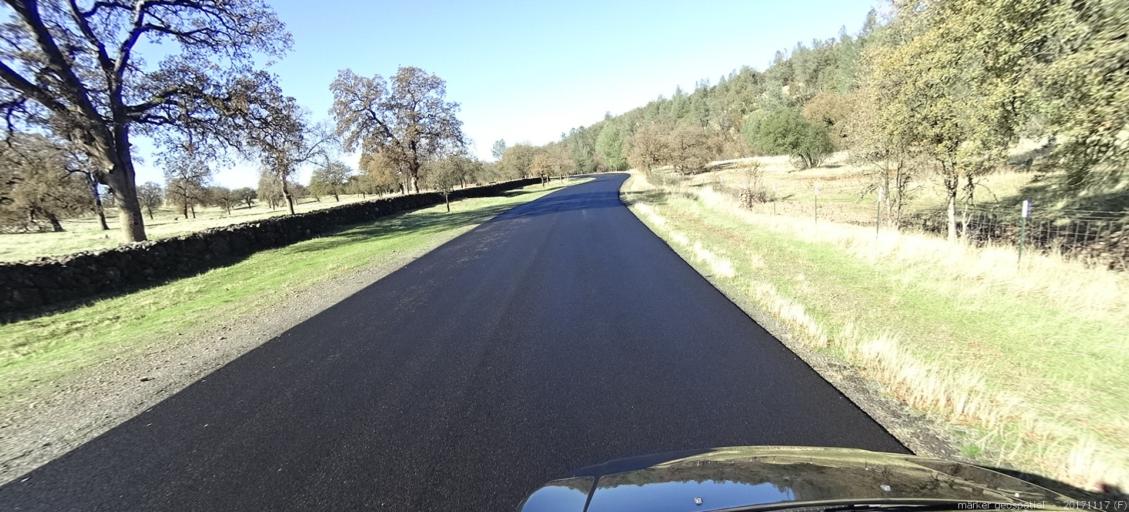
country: US
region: California
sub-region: Shasta County
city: Cottonwood
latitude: 40.4409
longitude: -122.1516
